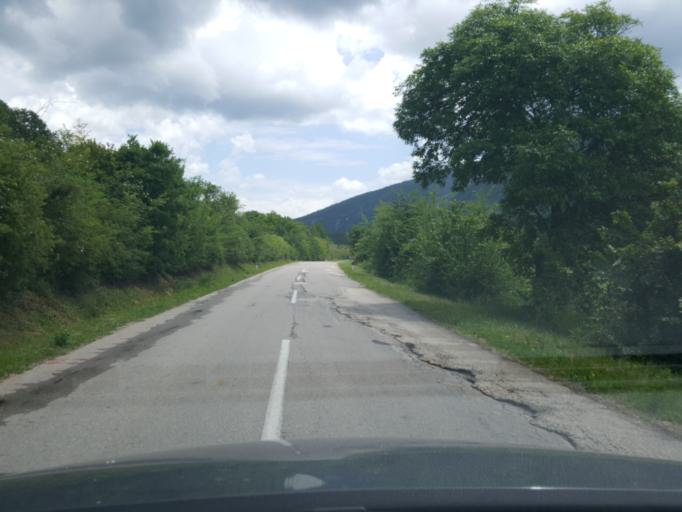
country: RS
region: Central Serbia
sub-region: Zajecarski Okrug
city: Soko Banja
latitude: 43.6393
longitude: 21.9619
